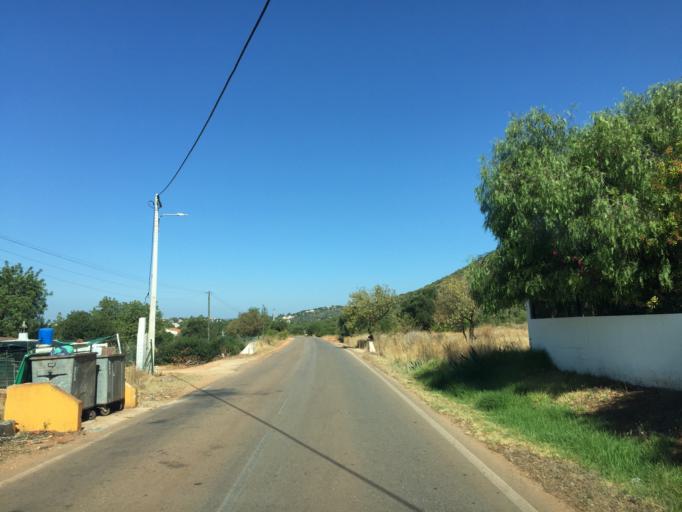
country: PT
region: Faro
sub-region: Loule
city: Almancil
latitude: 37.1079
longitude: -8.0647
